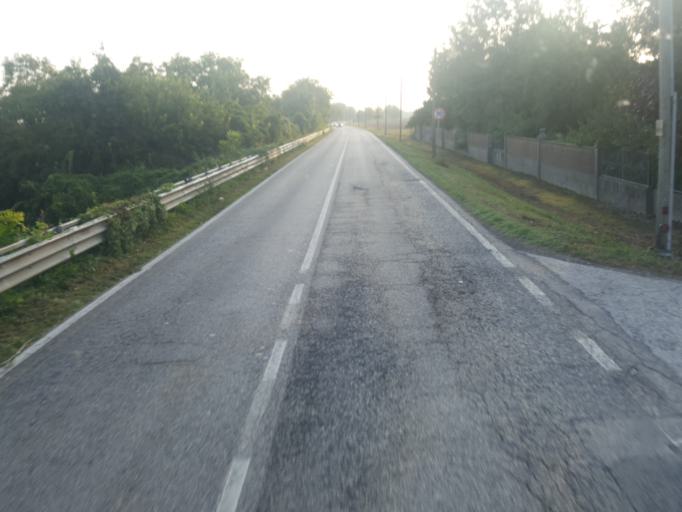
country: IT
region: Emilia-Romagna
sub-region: Provincia di Ferrara
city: San Biagio
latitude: 44.5798
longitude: 11.8840
